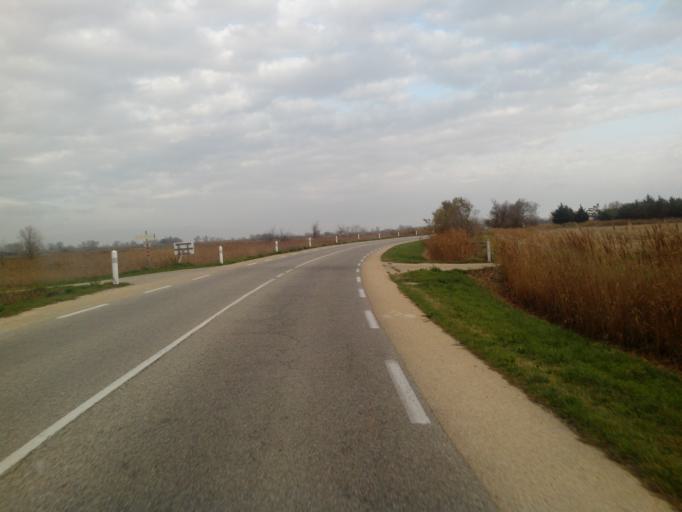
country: FR
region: Languedoc-Roussillon
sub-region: Departement du Gard
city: Saint-Gilles
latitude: 43.5720
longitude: 4.4204
